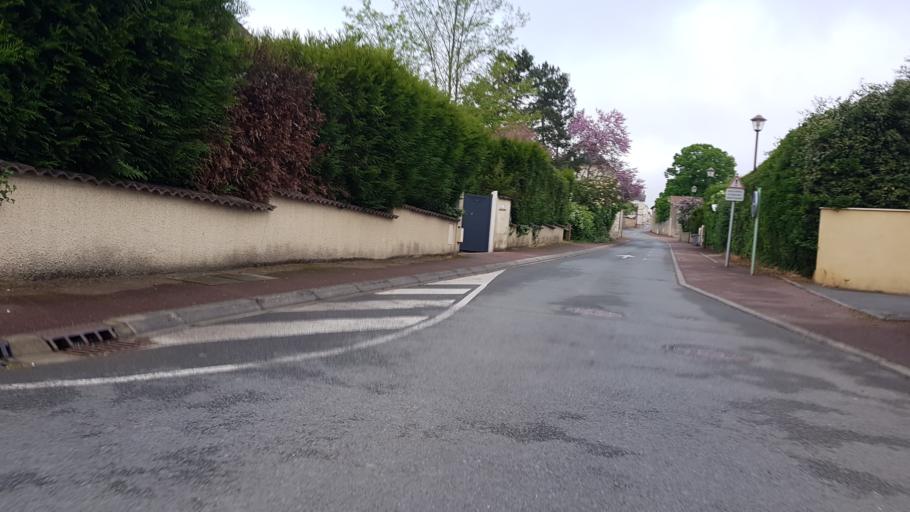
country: FR
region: Poitou-Charentes
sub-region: Departement de la Vienne
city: Jaunay-Clan
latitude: 46.6750
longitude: 0.3720
